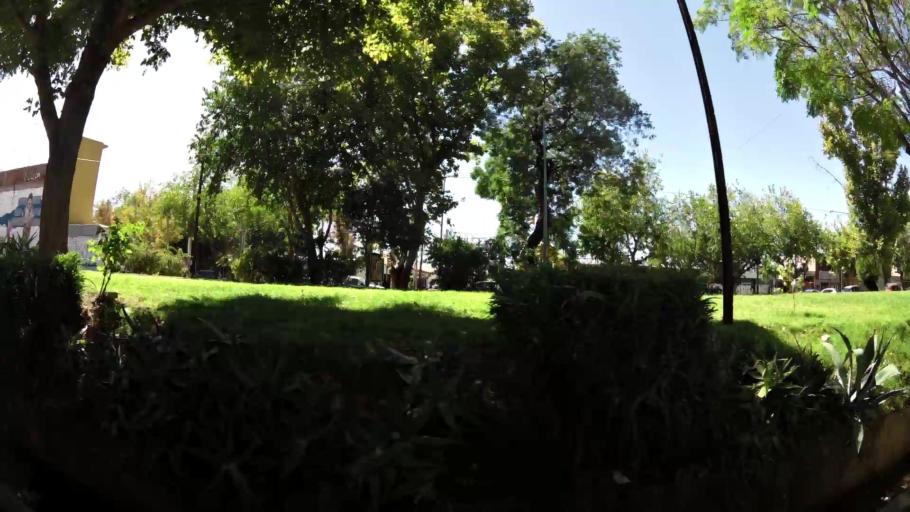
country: AR
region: Mendoza
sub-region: Departamento de Godoy Cruz
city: Godoy Cruz
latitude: -32.9391
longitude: -68.8506
